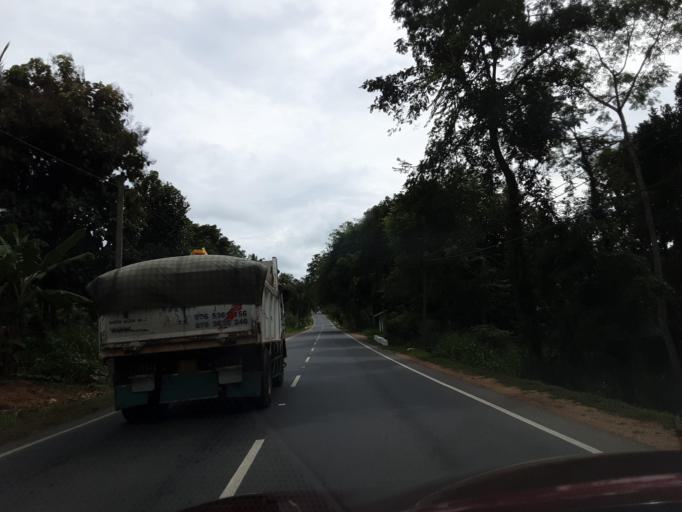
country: LK
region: Eastern Province
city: Eravur Town
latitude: 7.5211
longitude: 81.3446
